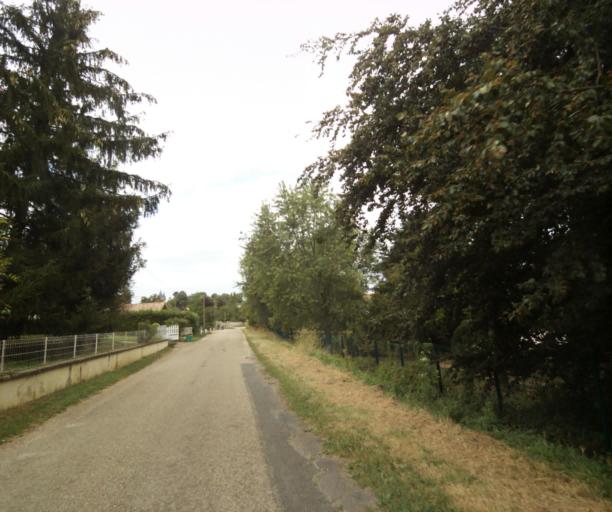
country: FR
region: Bourgogne
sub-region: Departement de Saone-et-Loire
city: Tournus
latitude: 46.5646
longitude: 4.8913
